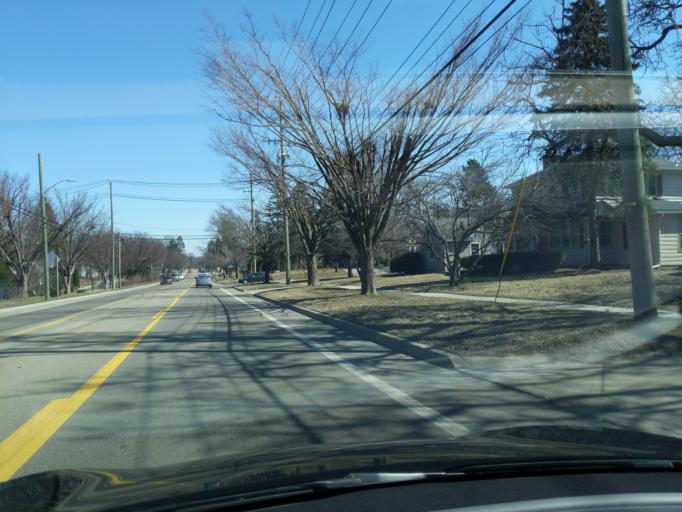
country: US
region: Michigan
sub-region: Washtenaw County
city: Ann Arbor
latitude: 42.2808
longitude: -83.7758
